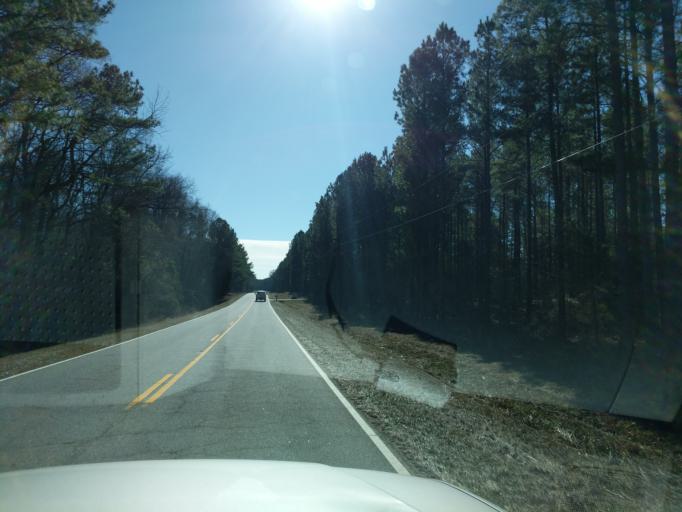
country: US
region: South Carolina
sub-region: Saluda County
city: Saluda
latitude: 34.1321
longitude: -81.8418
